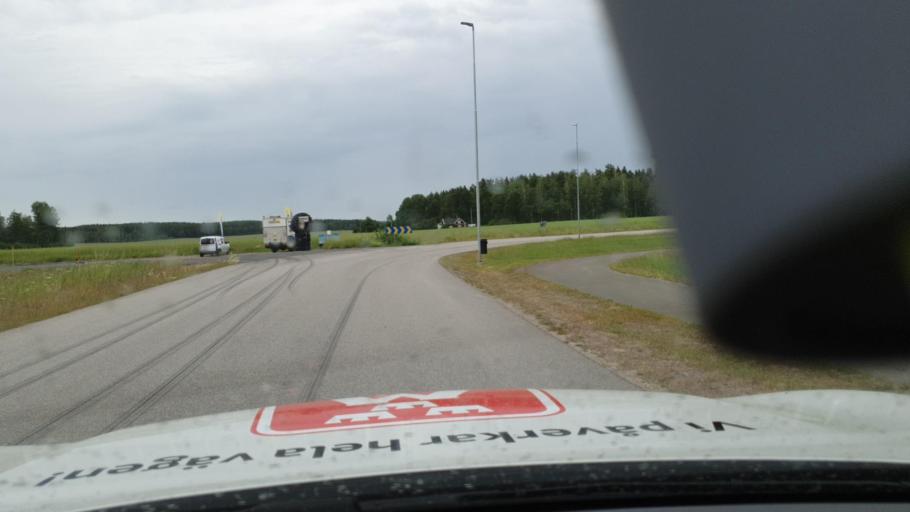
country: SE
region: Vaestra Goetaland
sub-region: Hjo Kommun
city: Hjo
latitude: 58.3169
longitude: 14.3002
